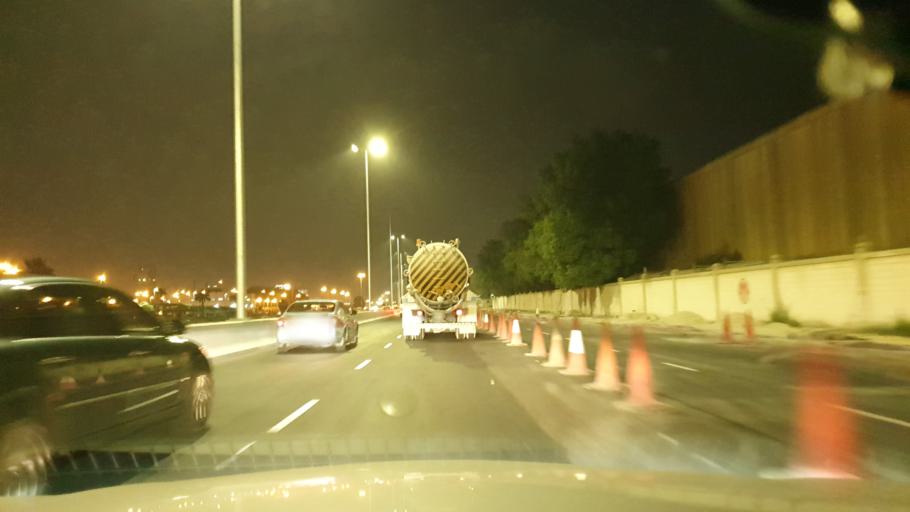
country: BH
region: Northern
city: Sitrah
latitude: 26.0829
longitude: 50.6127
